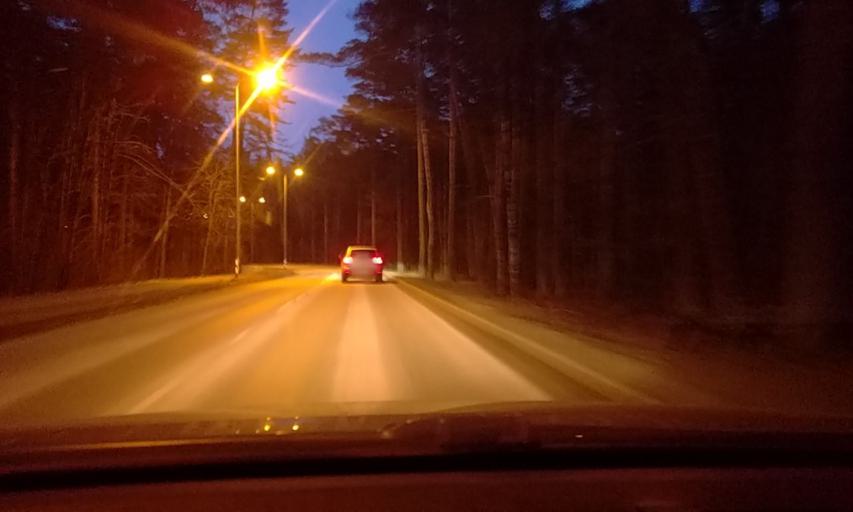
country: EE
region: Harju
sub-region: Viimsi vald
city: Viimsi
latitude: 59.4749
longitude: 24.8438
